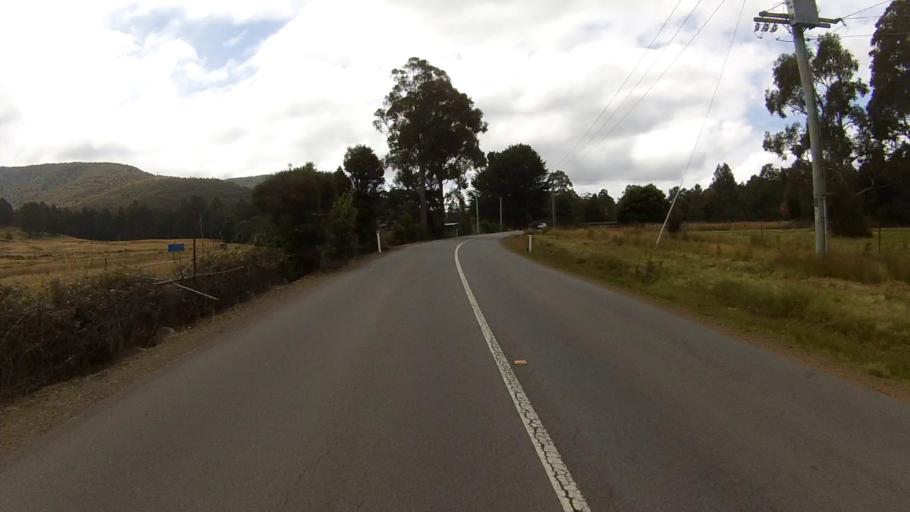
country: AU
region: Tasmania
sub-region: Kingborough
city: Kettering
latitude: -43.1191
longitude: 147.1858
